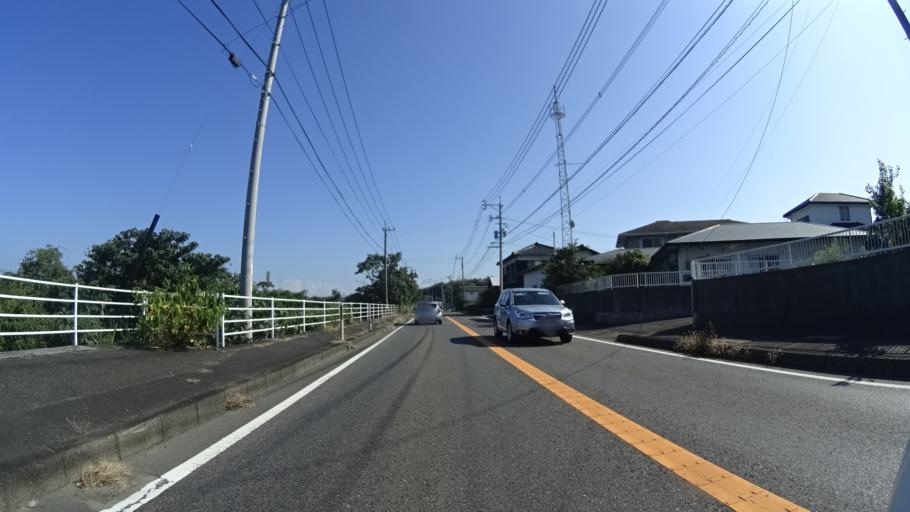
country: JP
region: Fukuoka
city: Shiida
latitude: 33.6428
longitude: 131.0688
